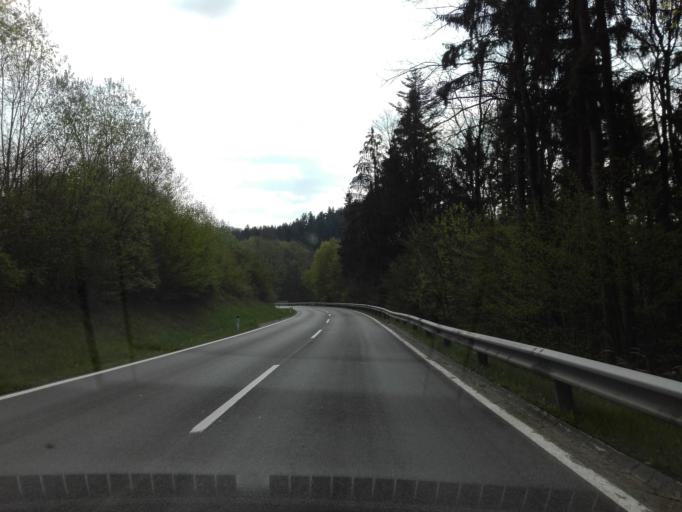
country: AT
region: Upper Austria
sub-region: Politischer Bezirk Perg
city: Perg
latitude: 48.2684
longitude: 14.6819
